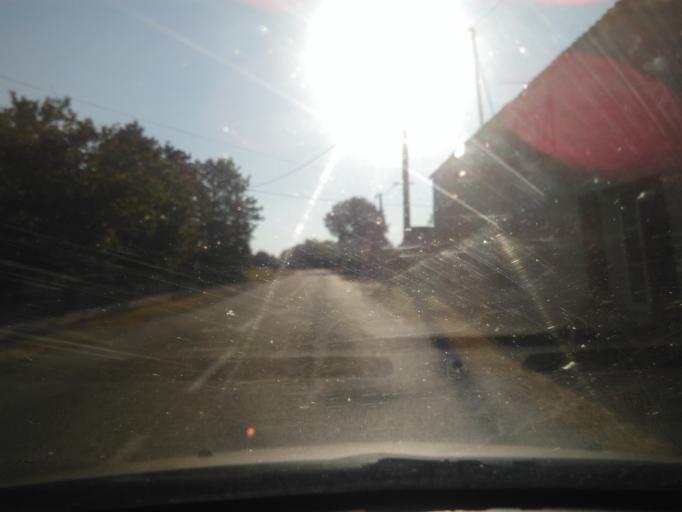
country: FR
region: Pays de la Loire
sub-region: Departement de la Vendee
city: Dompierre-sur-Yon
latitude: 46.7390
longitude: -1.4087
